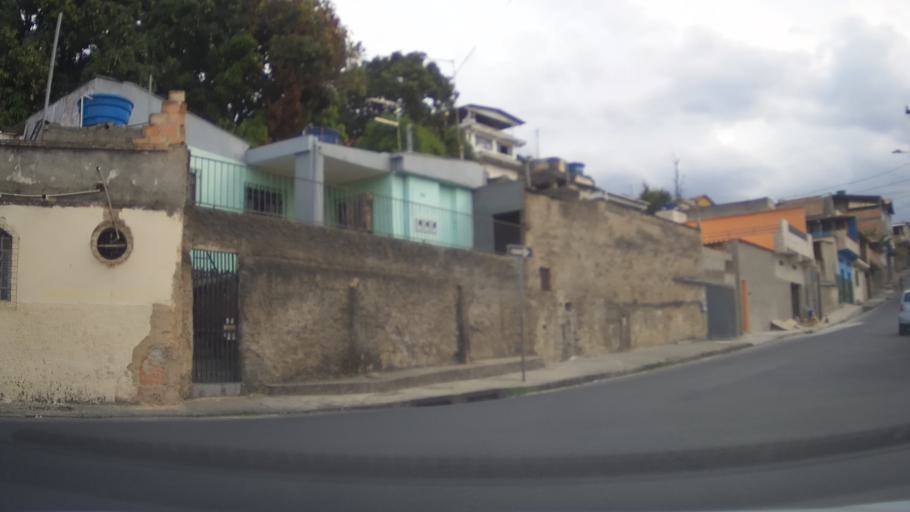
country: BR
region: Minas Gerais
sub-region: Belo Horizonte
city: Belo Horizonte
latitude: -19.8674
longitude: -43.8977
